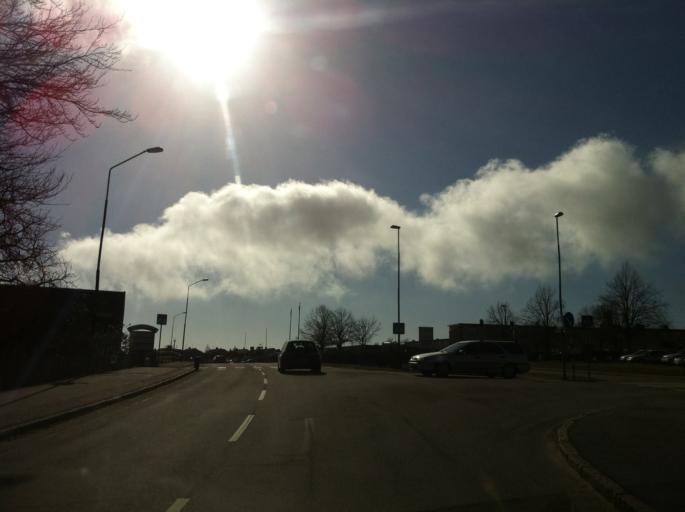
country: SE
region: Skane
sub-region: Bastads Kommun
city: Forslov
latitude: 56.3492
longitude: 12.8170
